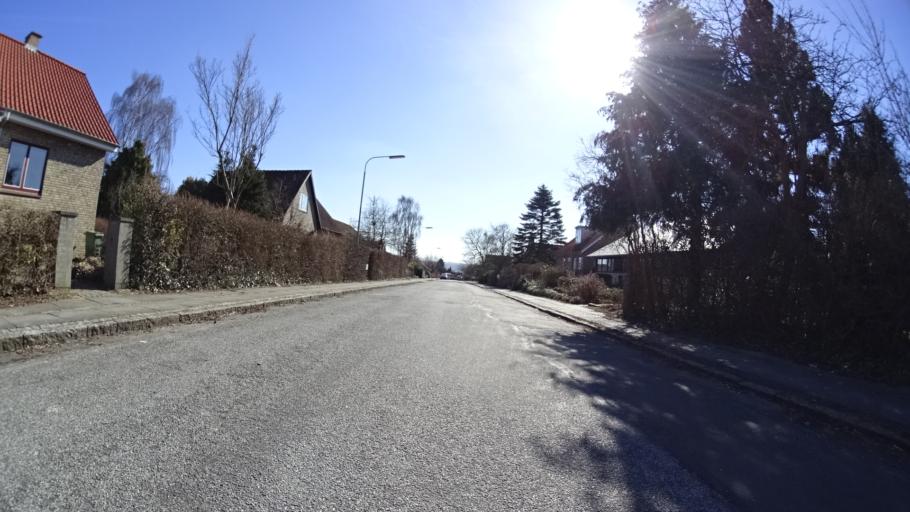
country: DK
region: Central Jutland
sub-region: Arhus Kommune
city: Arhus
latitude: 56.1705
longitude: 10.1700
